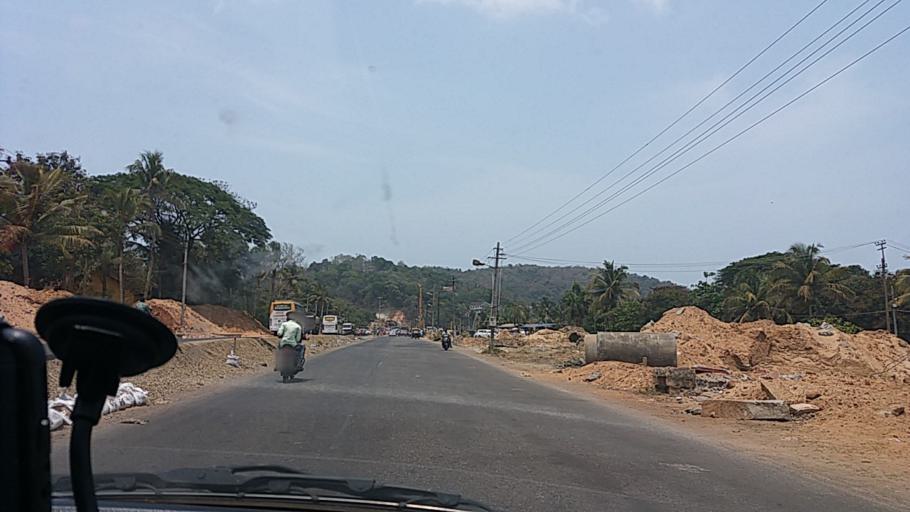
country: IN
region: Karnataka
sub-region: Uttar Kannada
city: Karwar
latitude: 14.8099
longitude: 74.1271
